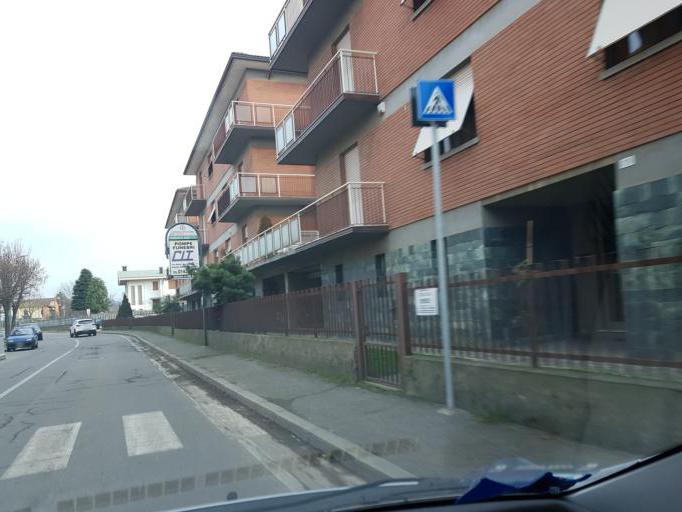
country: IT
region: Piedmont
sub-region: Provincia di Alessandria
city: Novi Ligure
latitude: 44.7621
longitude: 8.8047
